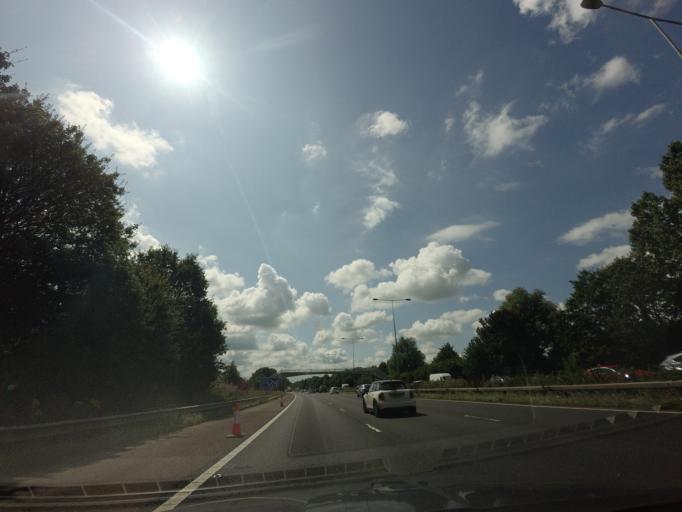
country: GB
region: England
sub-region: Lancashire
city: Clayton-le-Woods
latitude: 53.7051
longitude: -2.6765
